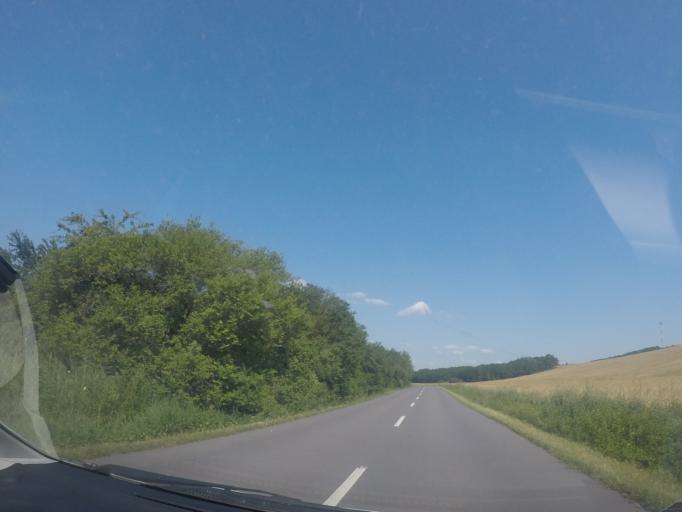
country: SK
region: Banskobystricky
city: Dudince
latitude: 48.1925
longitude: 18.8287
